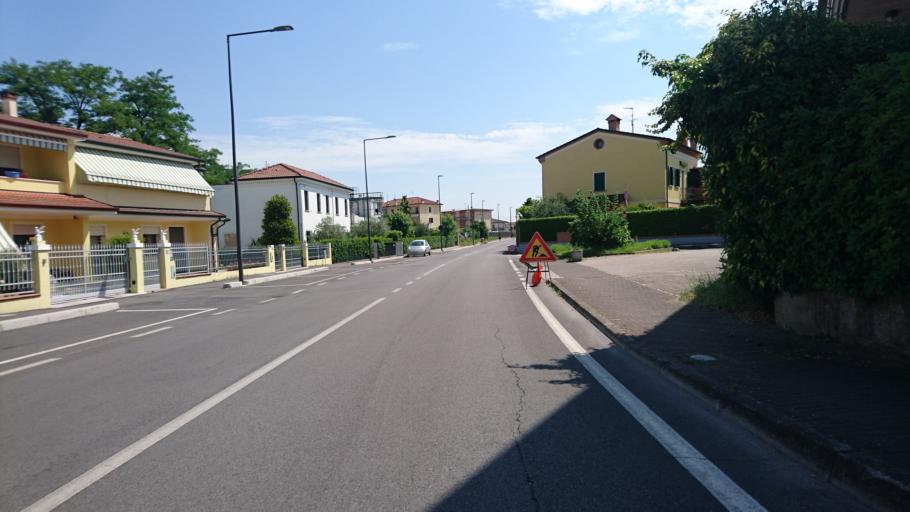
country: IT
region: Veneto
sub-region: Provincia di Padova
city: Ospedaletto Euganeo
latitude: 45.2213
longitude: 11.6084
